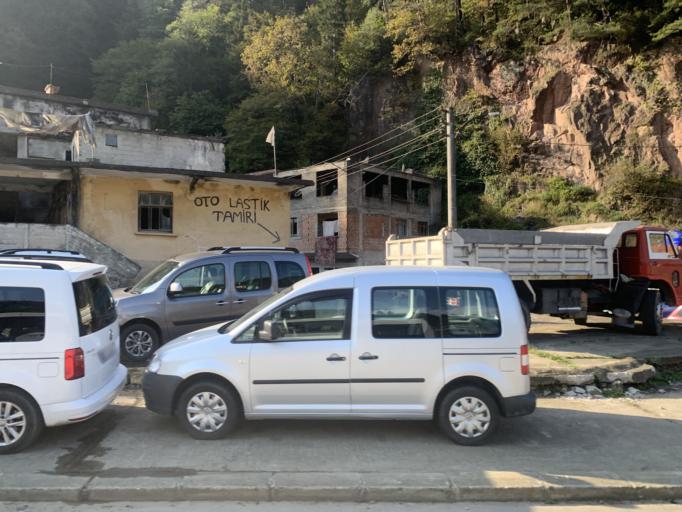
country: TR
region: Trabzon
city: Dernekpazari
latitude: 40.8409
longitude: 40.2800
